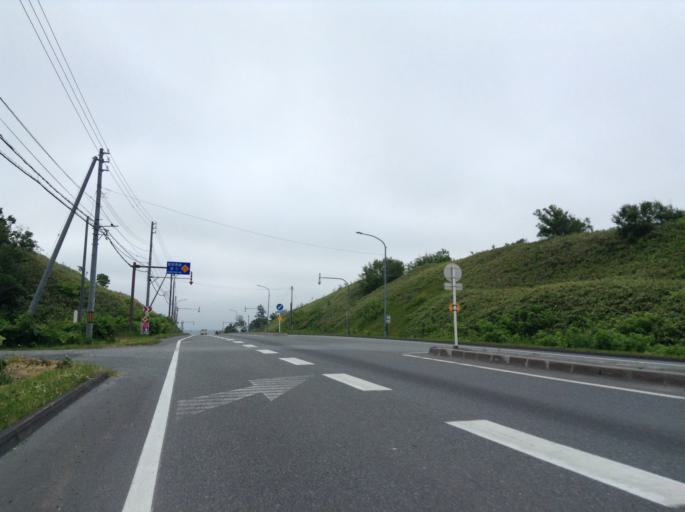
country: JP
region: Hokkaido
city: Wakkanai
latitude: 45.3742
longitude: 141.7155
